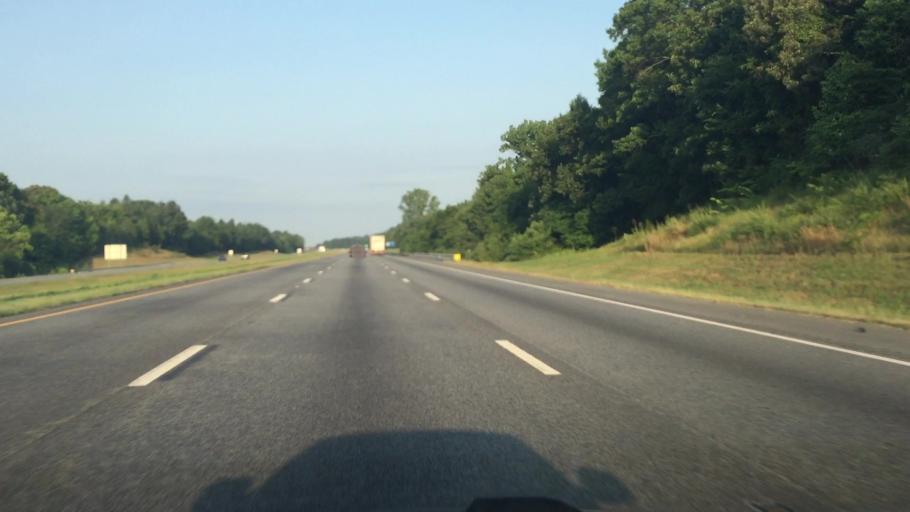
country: US
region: North Carolina
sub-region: Davidson County
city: Lexington
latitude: 35.8013
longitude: -80.2006
